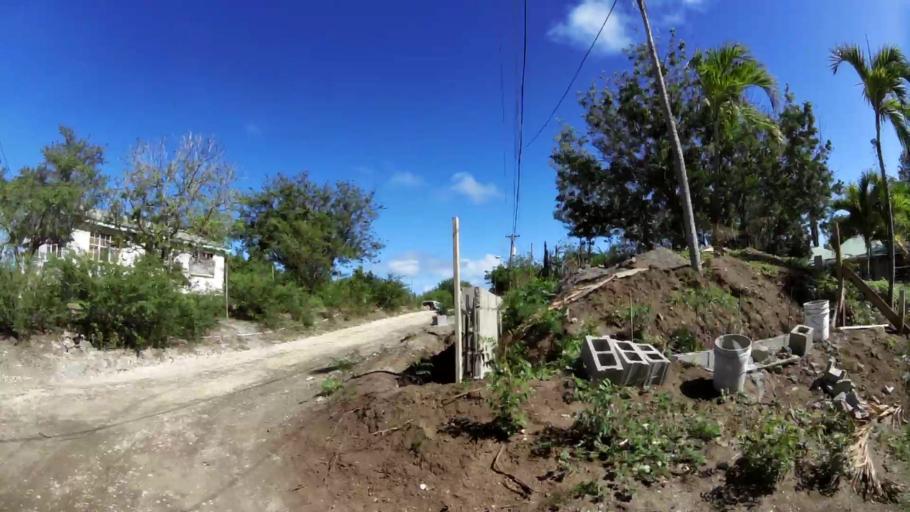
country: AG
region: Saint Paul
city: Falmouth
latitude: 17.0139
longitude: -61.7666
